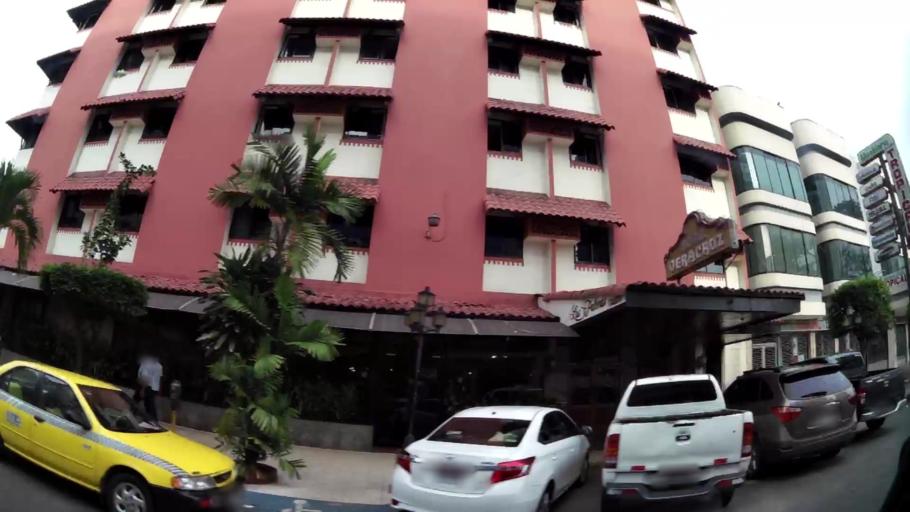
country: PA
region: Panama
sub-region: Distrito de Panama
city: Ancon
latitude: 8.9682
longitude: -79.5381
